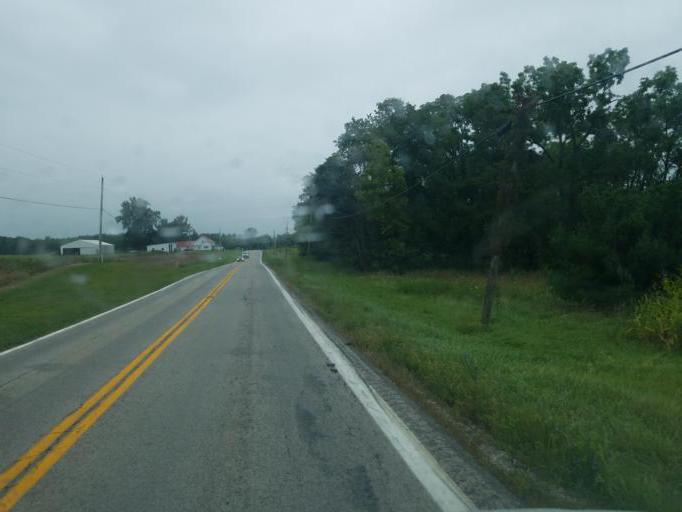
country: US
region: Ohio
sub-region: Knox County
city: Centerburg
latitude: 40.4587
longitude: -82.6964
